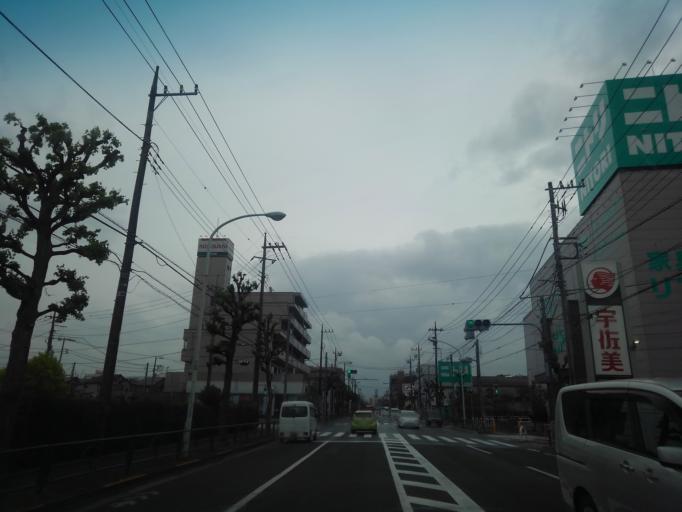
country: JP
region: Tokyo
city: Tanashicho
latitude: 35.7345
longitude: 139.5283
